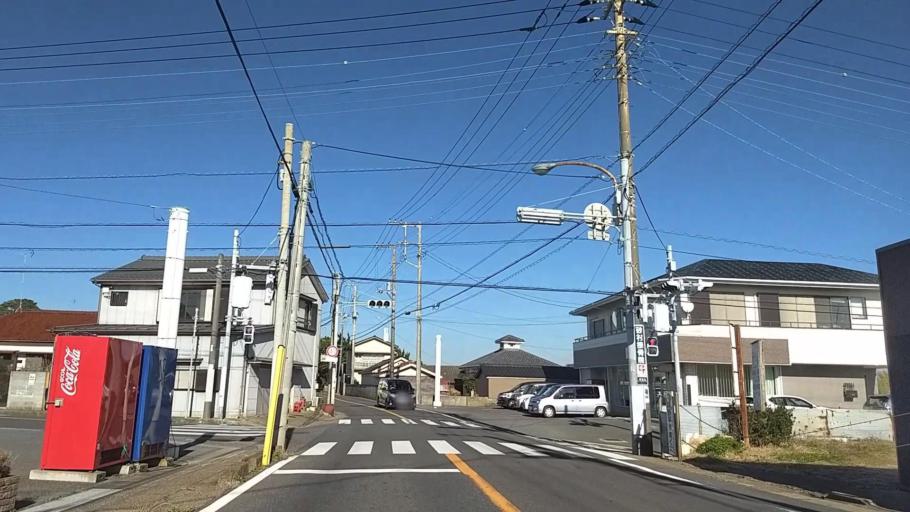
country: JP
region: Chiba
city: Hasaki
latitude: 35.7301
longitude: 140.8654
